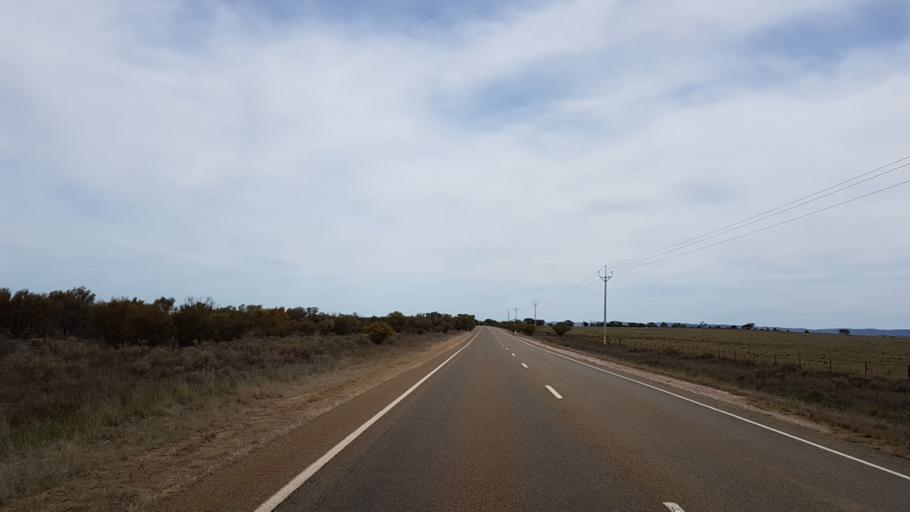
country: AU
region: South Australia
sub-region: Peterborough
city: Peterborough
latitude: -32.9894
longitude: 138.7944
